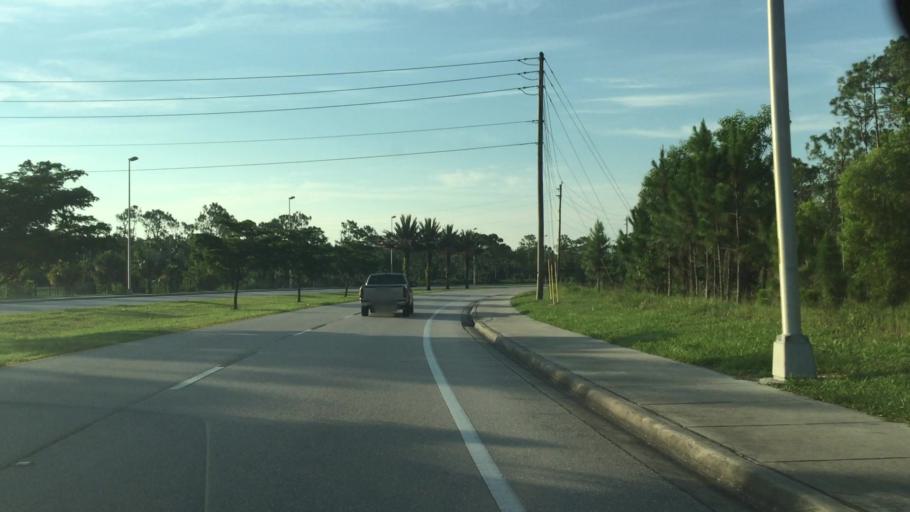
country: US
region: Florida
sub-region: Lee County
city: Three Oaks
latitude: 26.4663
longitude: -81.7910
